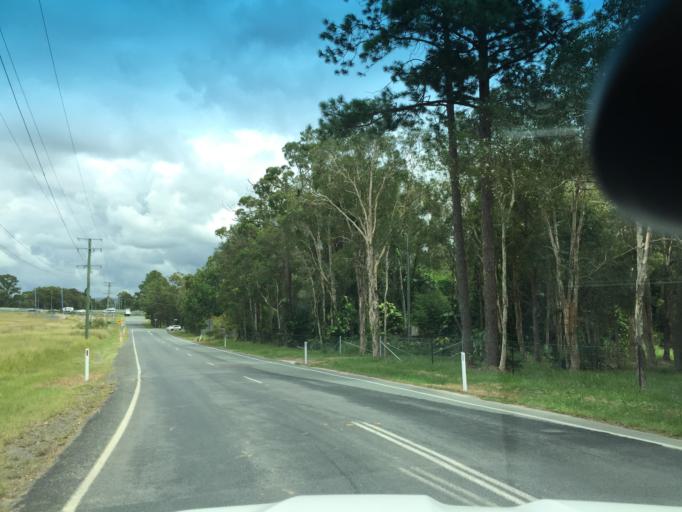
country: AU
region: Queensland
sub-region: Moreton Bay
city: Morayfield
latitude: -27.1100
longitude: 152.9805
